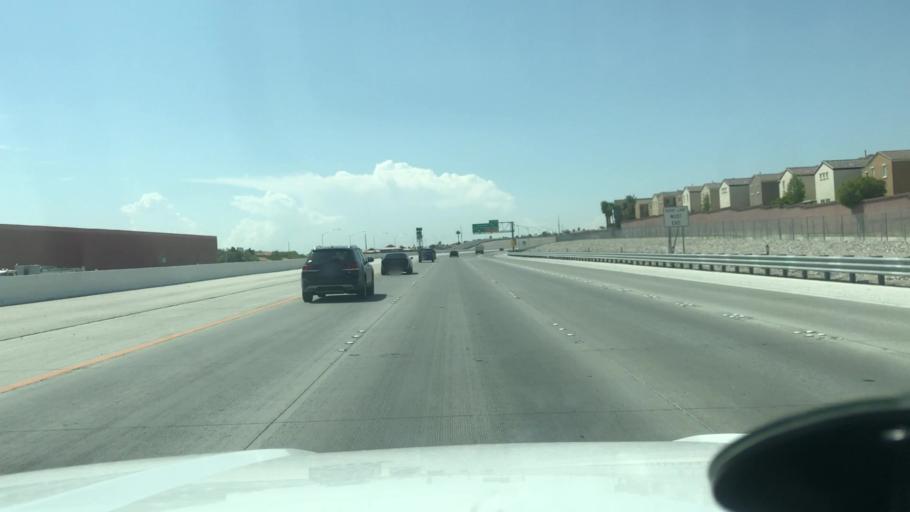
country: US
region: Nevada
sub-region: Clark County
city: Summerlin South
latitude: 36.2276
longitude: -115.3256
